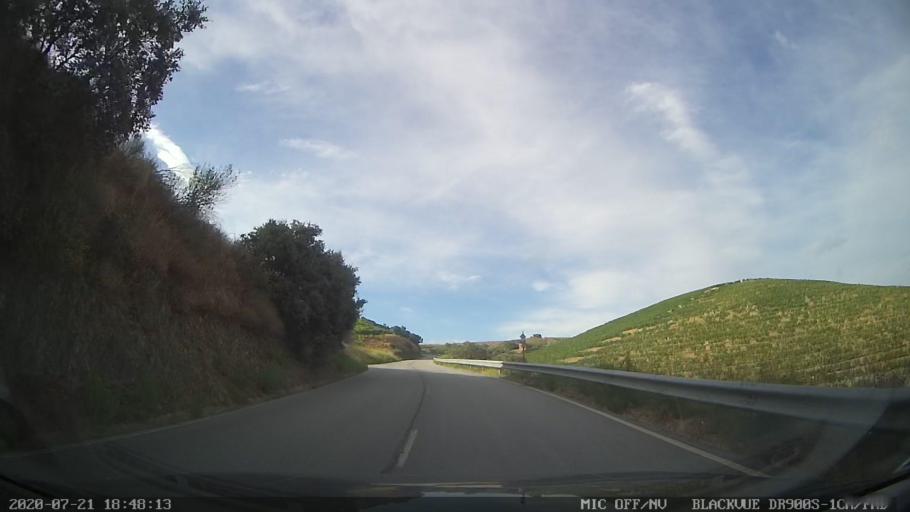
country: PT
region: Viseu
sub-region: Sao Joao da Pesqueira
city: Sao Joao da Pesqueira
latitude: 41.1267
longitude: -7.4364
